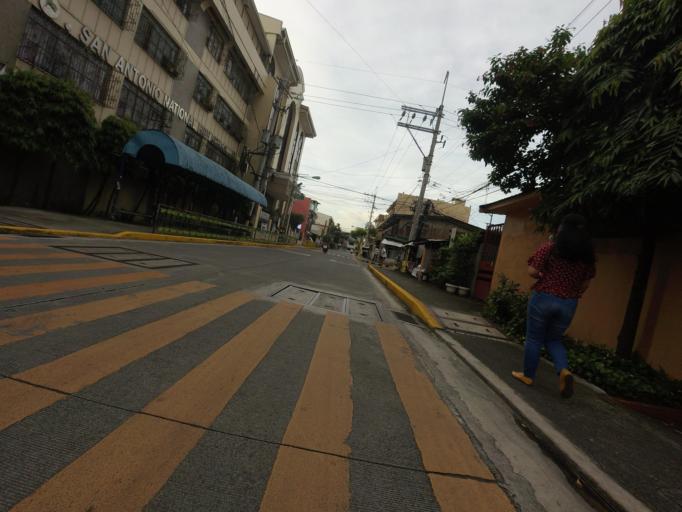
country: PH
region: Metro Manila
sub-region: Makati City
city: Makati City
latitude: 14.5611
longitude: 121.0065
